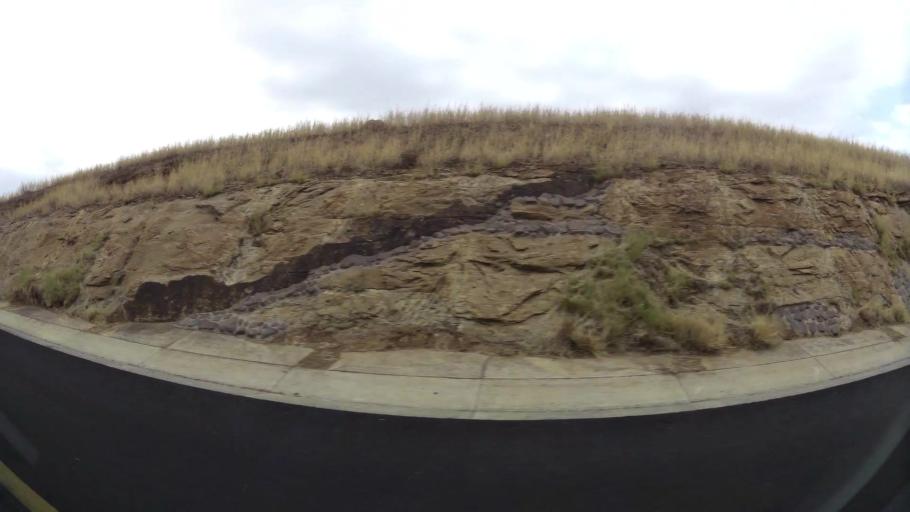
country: ZA
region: Orange Free State
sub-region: Fezile Dabi District Municipality
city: Kroonstad
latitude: -27.6457
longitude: 27.2476
